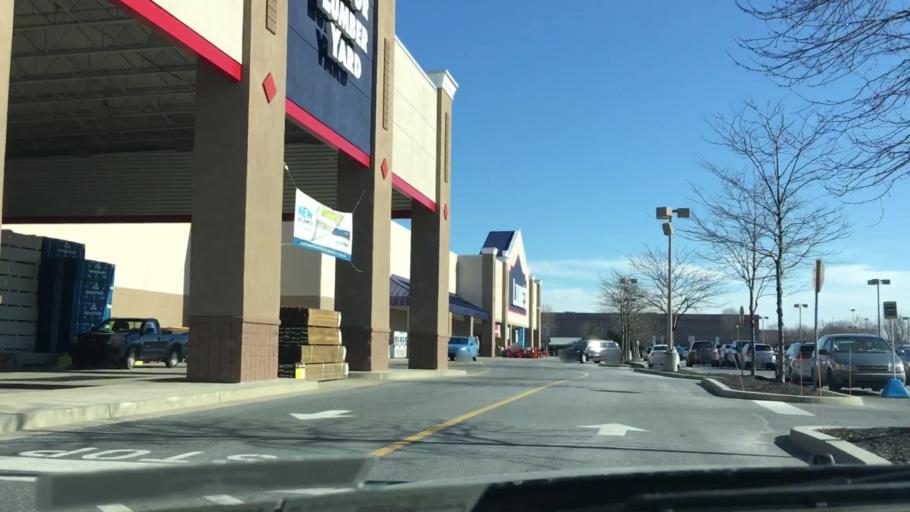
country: US
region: Pennsylvania
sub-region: Lancaster County
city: Lancaster
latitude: 40.0547
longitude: -76.2592
